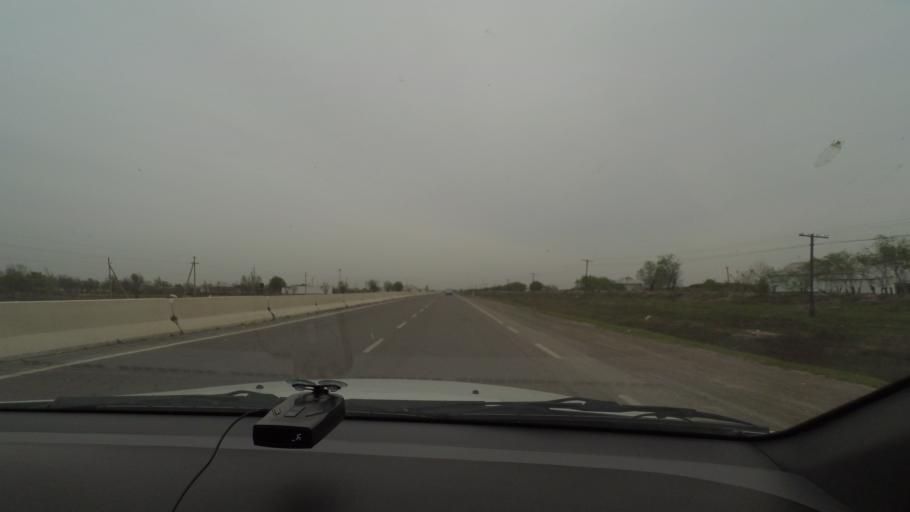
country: UZ
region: Sirdaryo
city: Guliston
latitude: 40.4962
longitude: 68.6224
